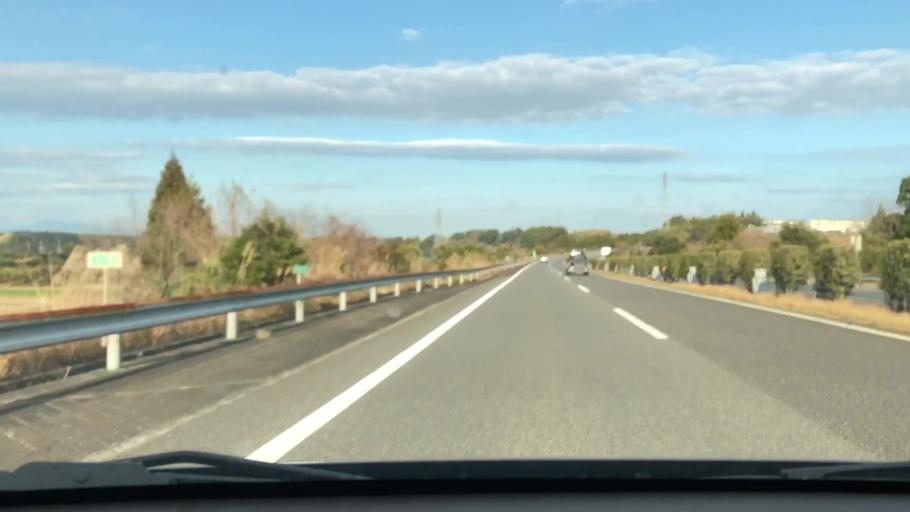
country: JP
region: Miyazaki
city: Miyazaki-shi
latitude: 31.8260
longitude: 131.3094
